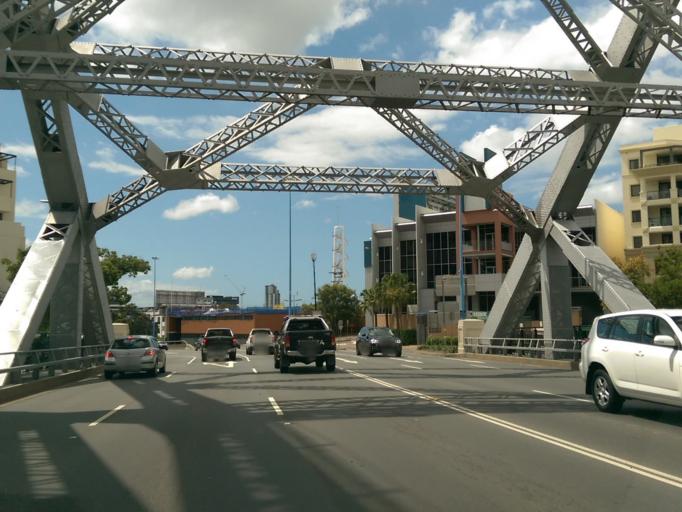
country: AU
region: Queensland
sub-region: Brisbane
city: Fortitude Valley
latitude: -27.4621
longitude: 153.0357
